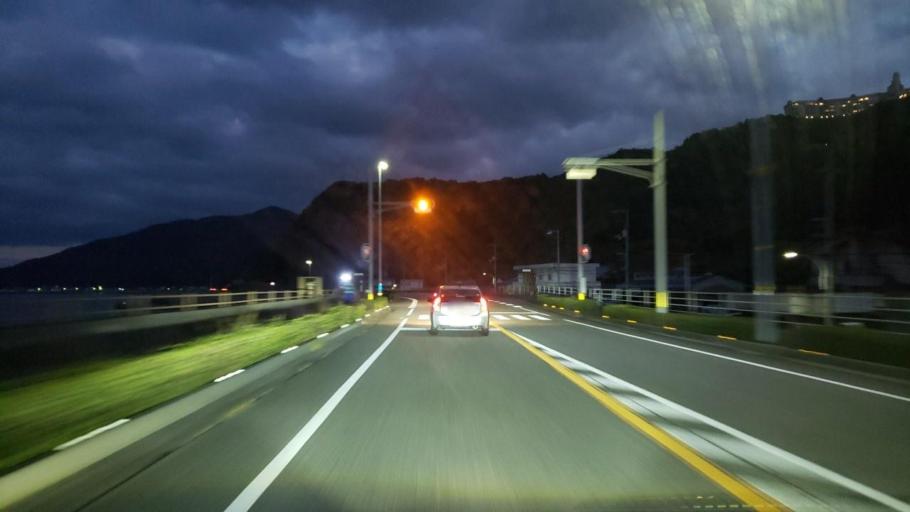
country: JP
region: Tokushima
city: Ishii
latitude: 34.2073
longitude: 134.4626
